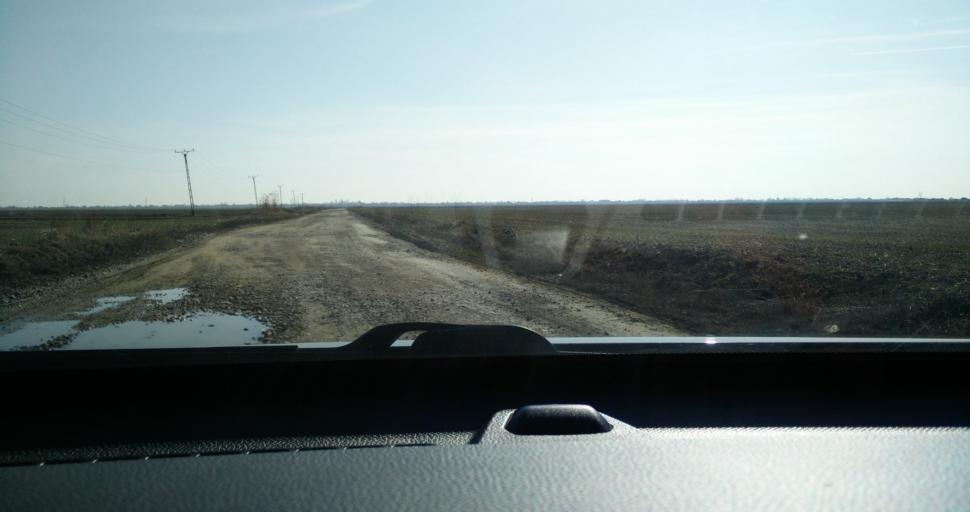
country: RO
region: Vrancea
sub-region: Comuna Suraia
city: Suraia
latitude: 45.6519
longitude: 27.3956
